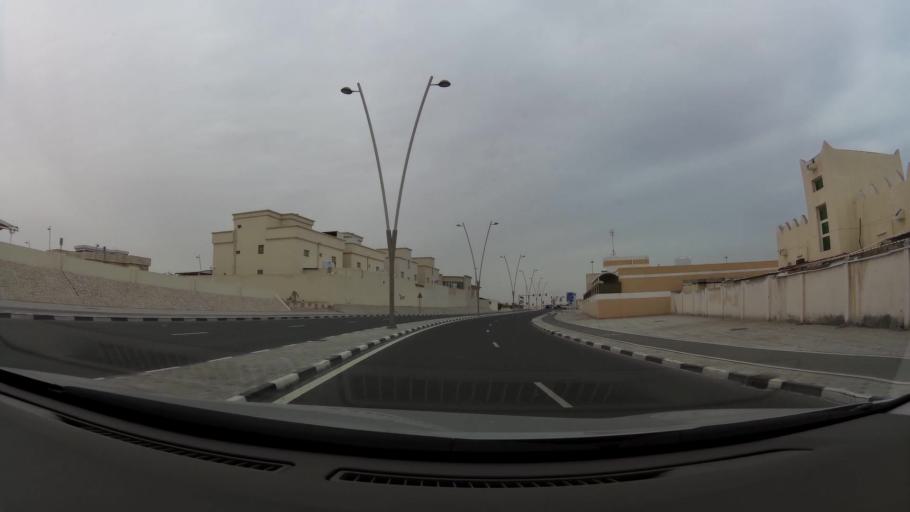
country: QA
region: Baladiyat ad Dawhah
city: Doha
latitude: 25.3462
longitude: 51.4884
